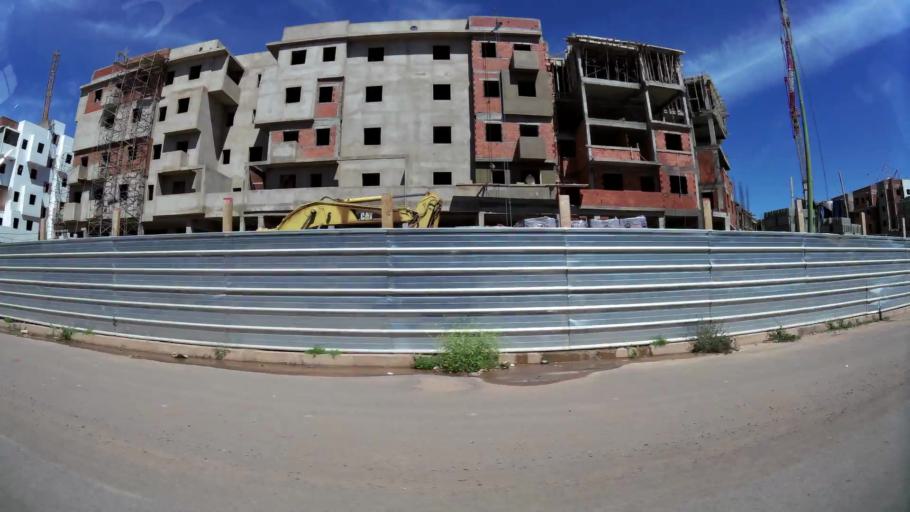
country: MA
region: Marrakech-Tensift-Al Haouz
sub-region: Marrakech
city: Marrakesh
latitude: 31.6343
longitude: -8.0743
